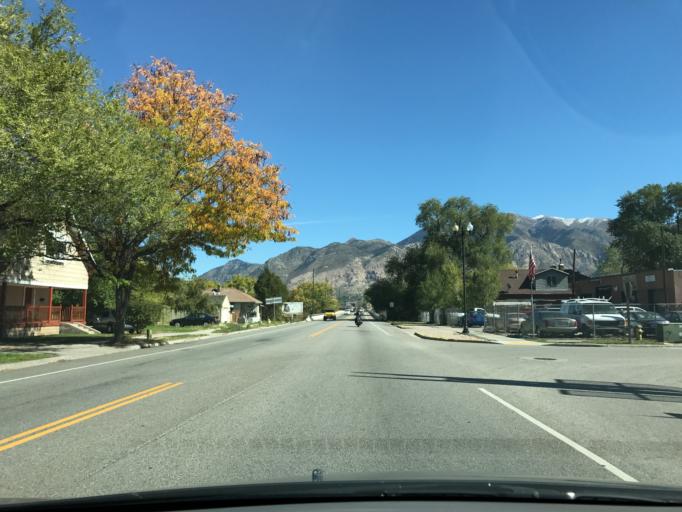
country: US
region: Utah
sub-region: Weber County
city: Ogden
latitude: 41.2230
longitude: -111.9902
